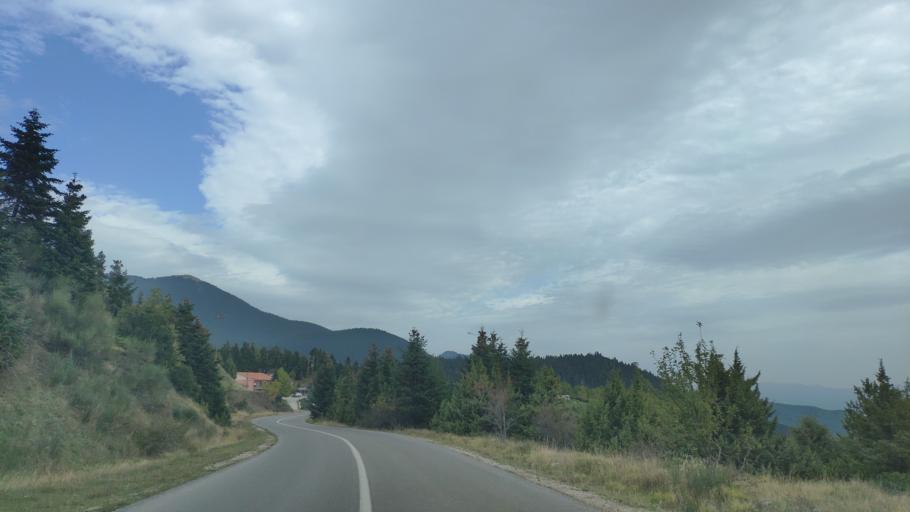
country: GR
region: Central Greece
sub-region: Nomos Fthiotidos
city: Stavros
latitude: 38.7147
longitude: 22.3263
